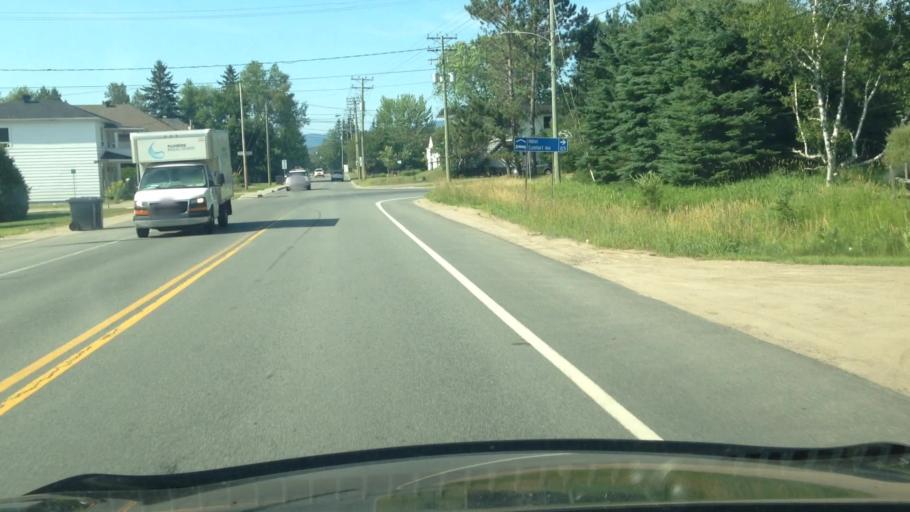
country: CA
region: Quebec
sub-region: Laurentides
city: Mont-Tremblant
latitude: 46.1143
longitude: -74.5955
